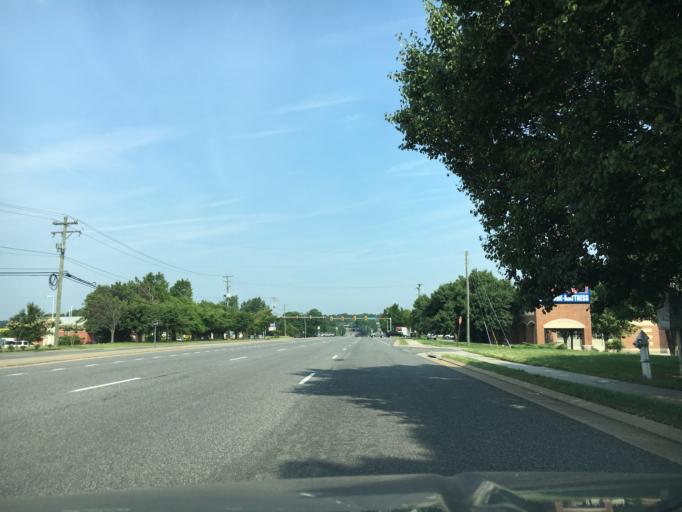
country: US
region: Virginia
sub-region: Henrico County
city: Short Pump
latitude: 37.6417
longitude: -77.5627
